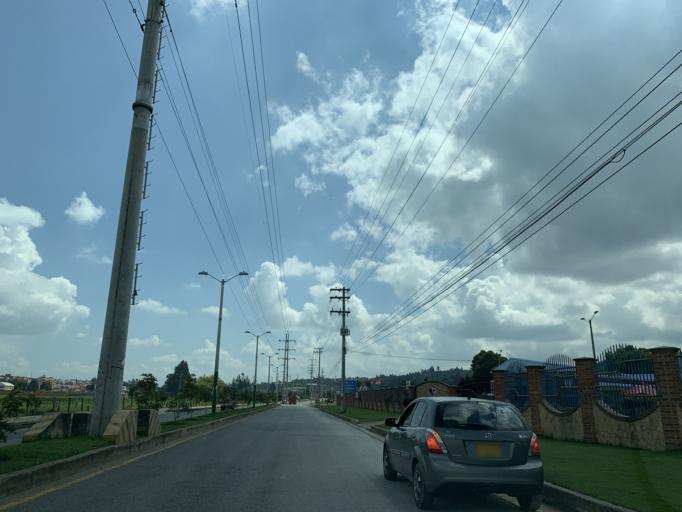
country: CO
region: Boyaca
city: Tunja
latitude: 5.5638
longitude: -73.3383
